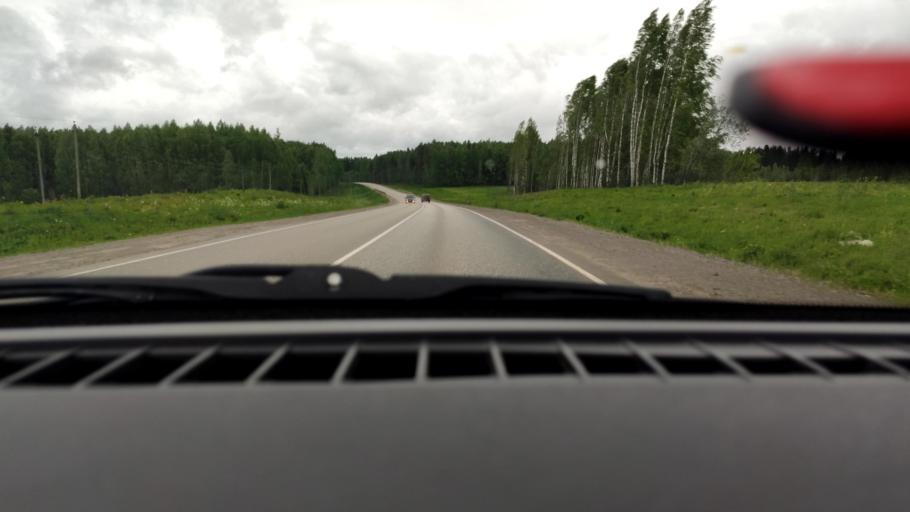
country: RU
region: Perm
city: Nytva
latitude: 57.9970
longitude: 55.2375
